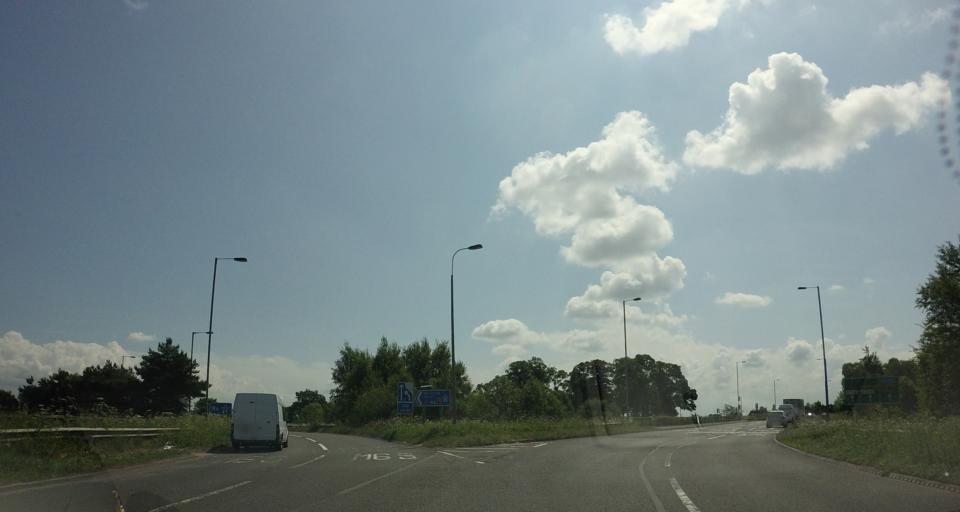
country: GB
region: England
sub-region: Cumbria
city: Carlisle
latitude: 54.9306
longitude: -2.9452
